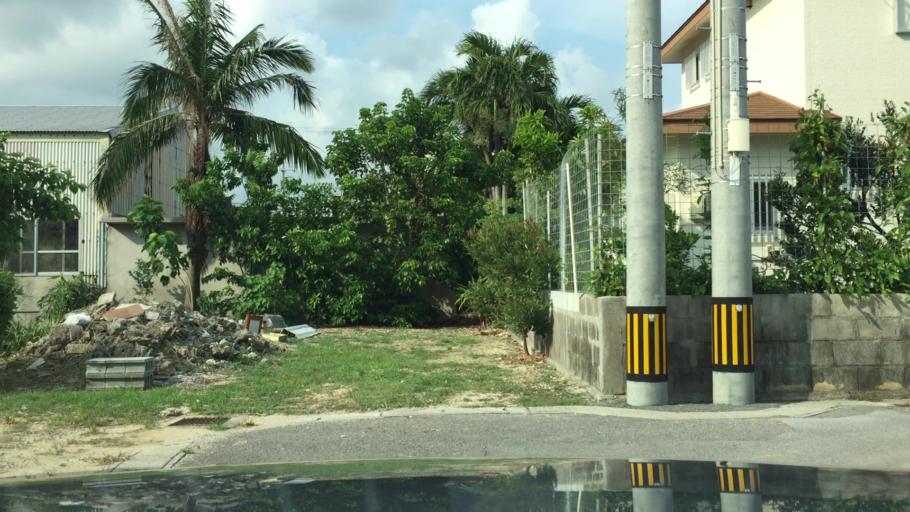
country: JP
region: Okinawa
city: Ishigaki
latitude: 24.3484
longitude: 124.1617
